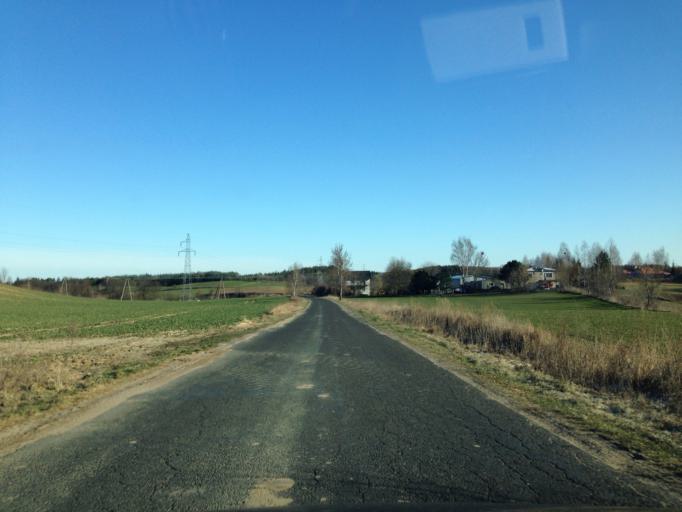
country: PL
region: Warmian-Masurian Voivodeship
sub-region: Powiat nowomiejski
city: Nowe Miasto Lubawskie
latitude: 53.4009
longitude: 19.6080
